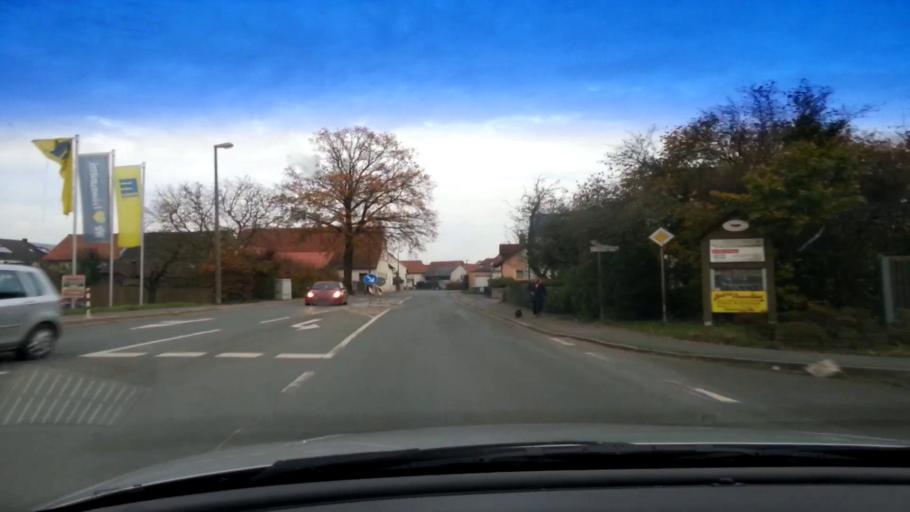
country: DE
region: Bavaria
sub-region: Upper Franconia
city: Breitengussbach
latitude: 49.9726
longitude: 10.8824
